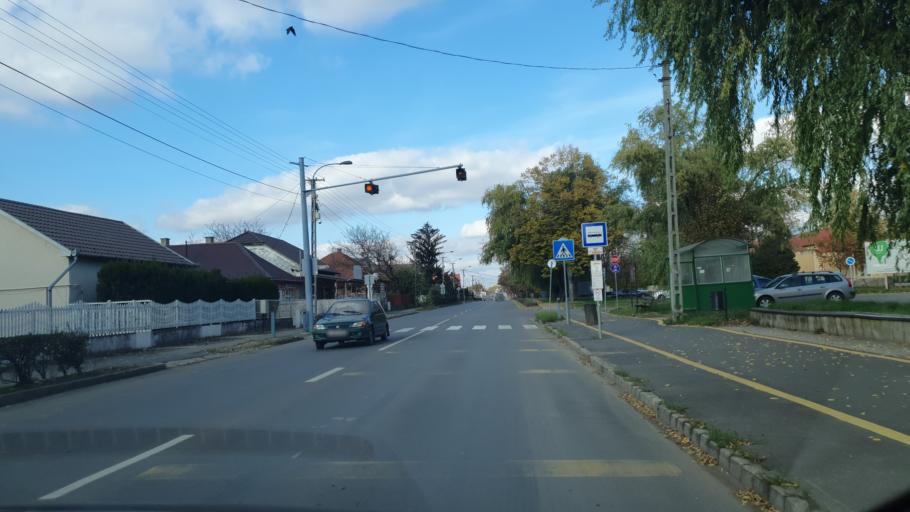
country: HU
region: Szabolcs-Szatmar-Bereg
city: Kisvarda
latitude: 48.2079
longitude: 22.0883
